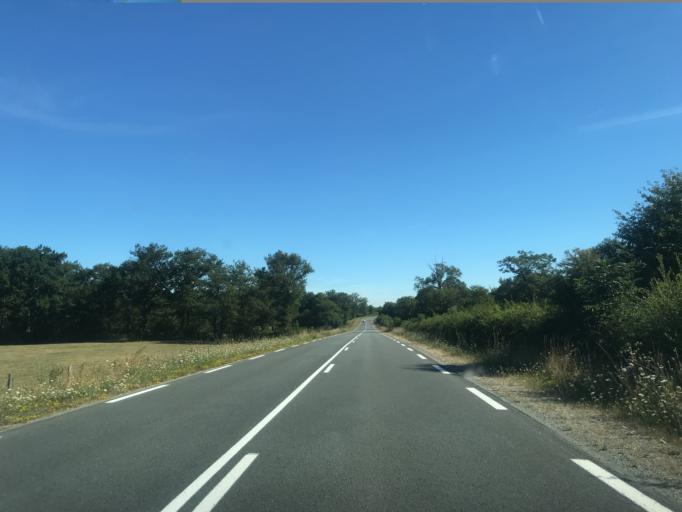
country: FR
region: Limousin
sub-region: Departement de la Creuse
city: Gouzon
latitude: 46.1593
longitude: 2.2112
